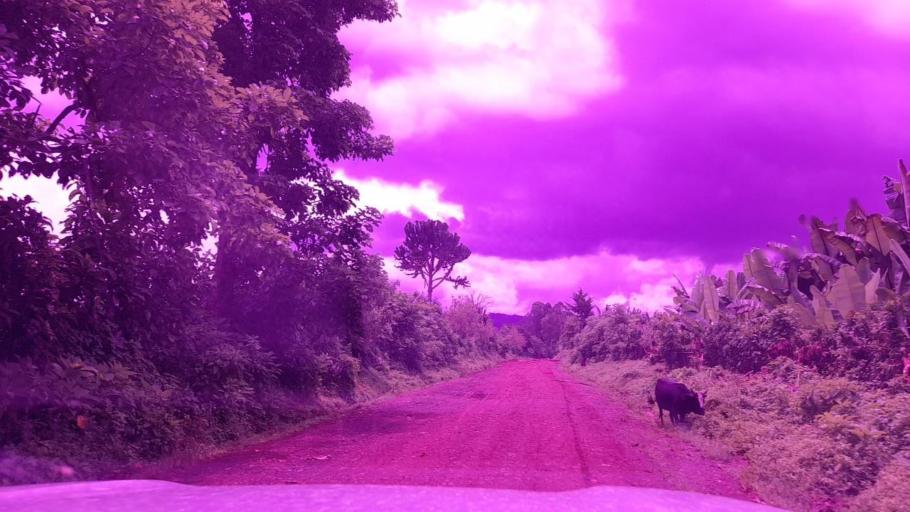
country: ET
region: Southern Nations, Nationalities, and People's Region
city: Tippi
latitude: 7.6287
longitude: 35.5797
